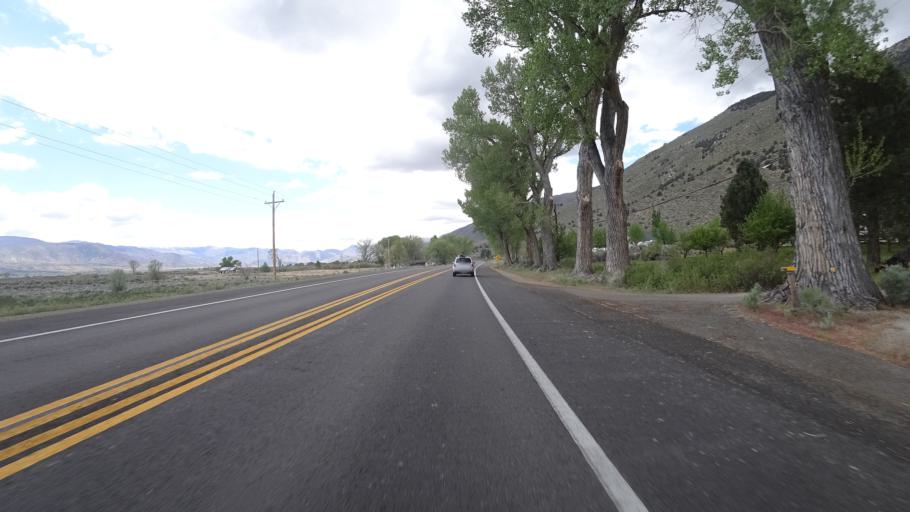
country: US
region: Nevada
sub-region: Lyon County
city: Smith Valley
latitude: 38.6132
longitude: -119.5195
